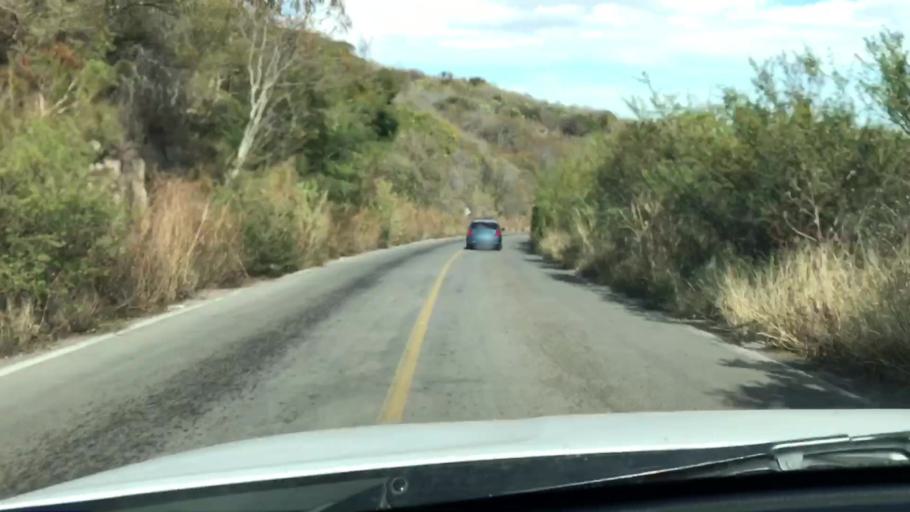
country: MX
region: Jalisco
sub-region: Zacoalco de Torres
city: Barranca de Otates (Barranca de Otatan)
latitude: 20.2429
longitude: -103.6833
